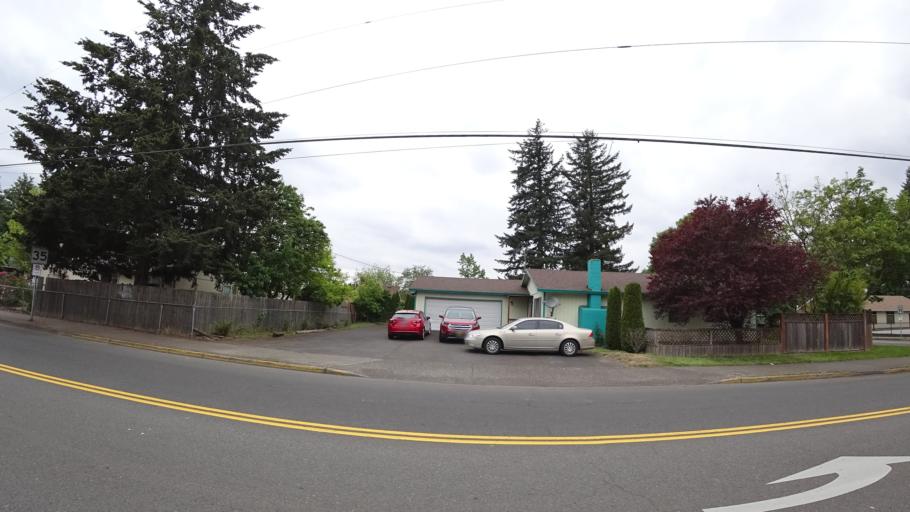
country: US
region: Oregon
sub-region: Multnomah County
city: Lents
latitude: 45.5113
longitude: -122.5481
